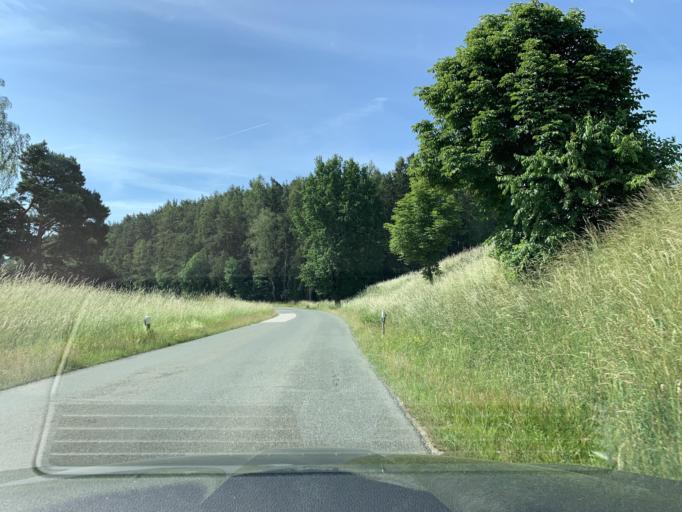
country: DE
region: Bavaria
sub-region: Upper Palatinate
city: Schwarzhofen
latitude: 49.3894
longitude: 12.3148
